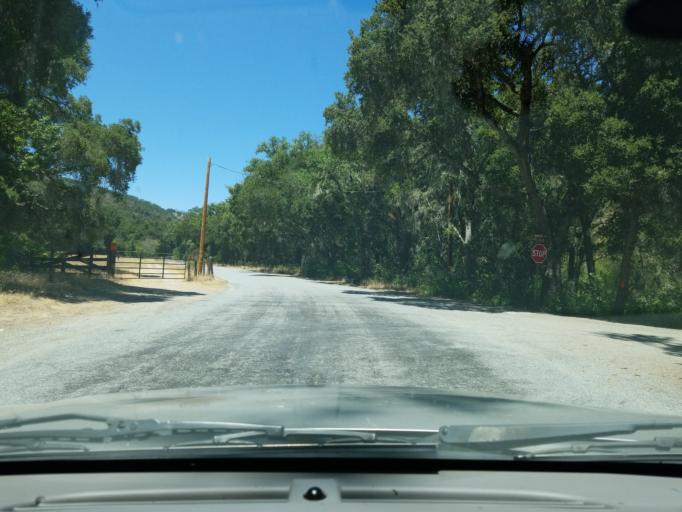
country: US
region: California
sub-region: Monterey County
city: Gonzales
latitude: 36.3788
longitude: -121.5643
